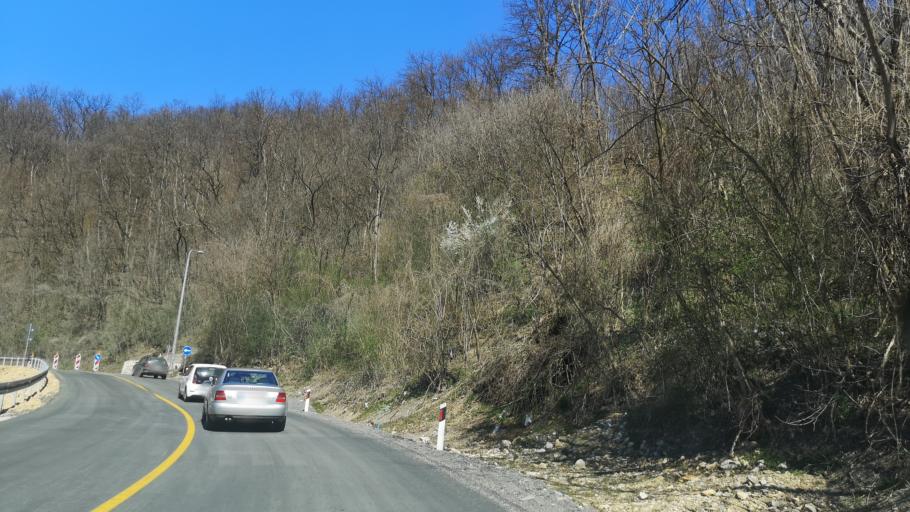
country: RS
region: Central Serbia
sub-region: Moravicki Okrug
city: Lucani
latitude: 43.8718
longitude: 20.1141
